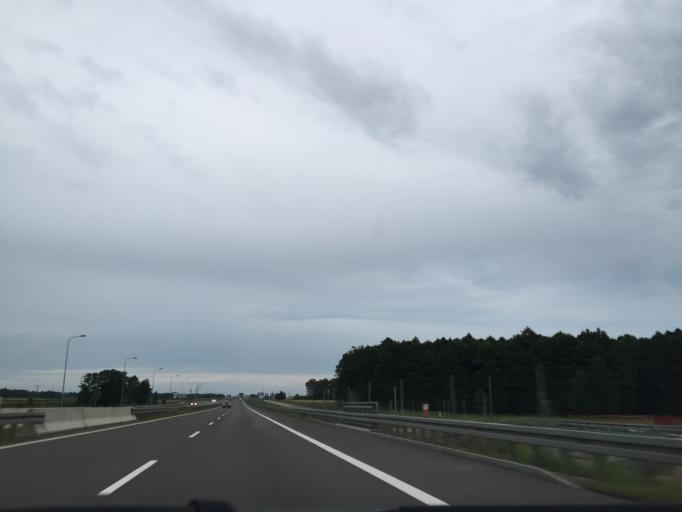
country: PL
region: Podlasie
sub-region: Powiat bialostocki
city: Choroszcz
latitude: 53.1574
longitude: 22.8810
